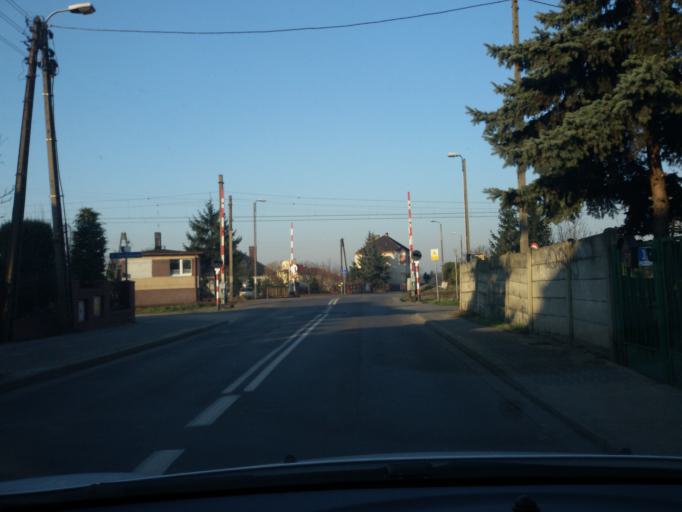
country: PL
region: Greater Poland Voivodeship
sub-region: Leszno
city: Leszno
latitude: 51.8331
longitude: 16.5745
